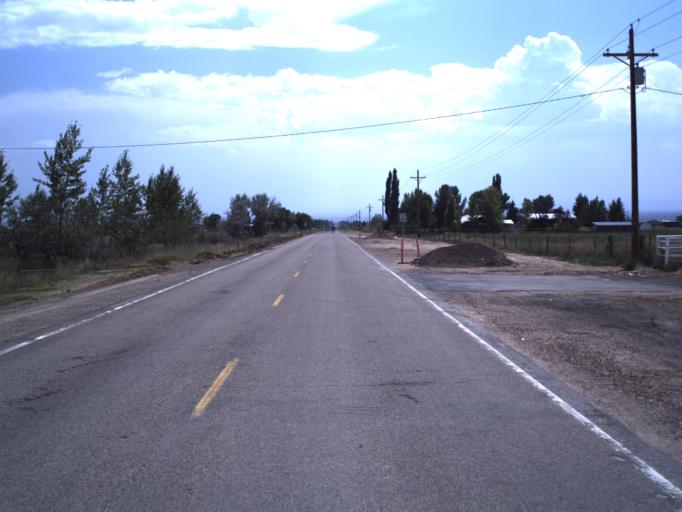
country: US
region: Utah
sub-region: Duchesne County
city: Roosevelt
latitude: 40.4256
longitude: -110.0300
